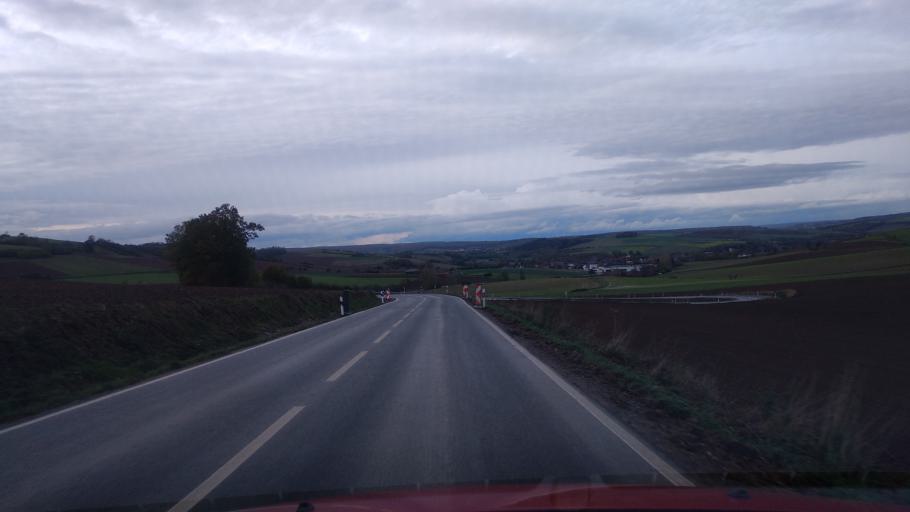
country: DE
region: North Rhine-Westphalia
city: Brakel
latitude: 51.6704
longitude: 9.2345
